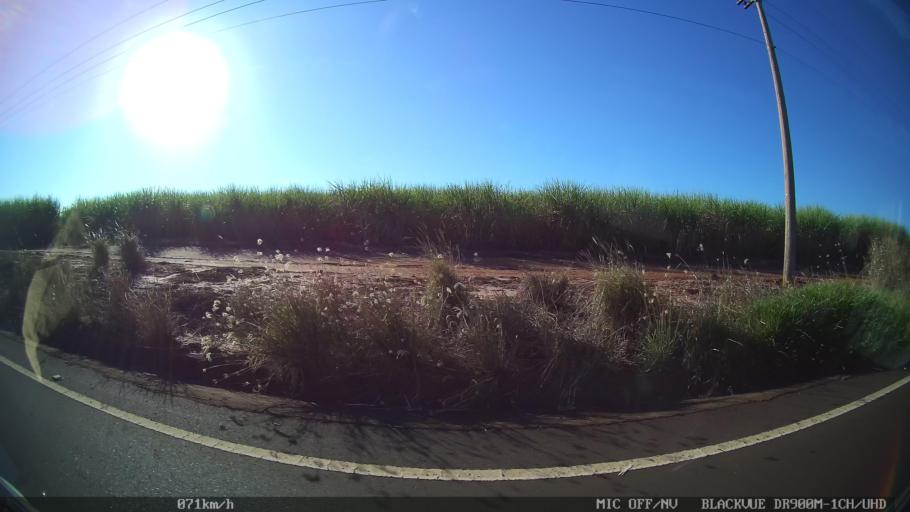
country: BR
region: Sao Paulo
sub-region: Guapiacu
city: Guapiacu
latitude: -20.7362
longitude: -49.0790
